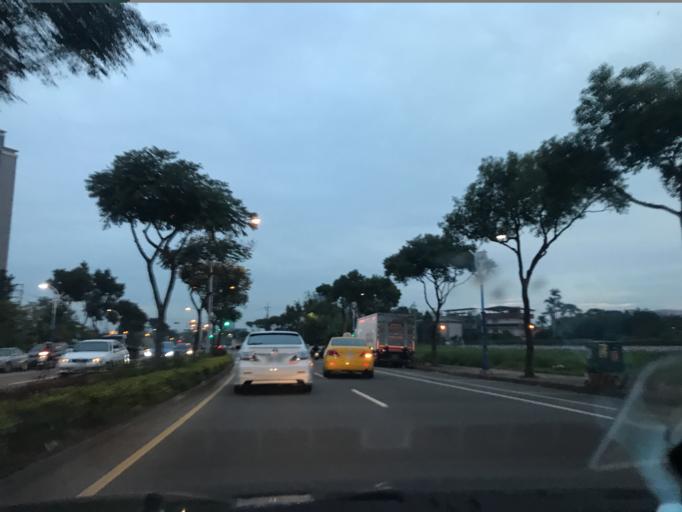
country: TW
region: Taiwan
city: Daxi
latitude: 24.9353
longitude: 121.2390
